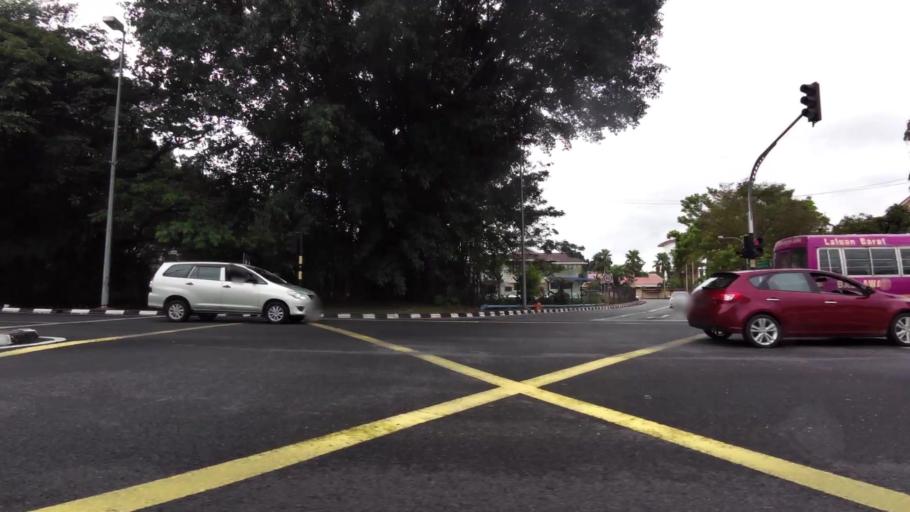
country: BN
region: Brunei and Muara
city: Bandar Seri Begawan
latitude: 4.9017
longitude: 114.9352
